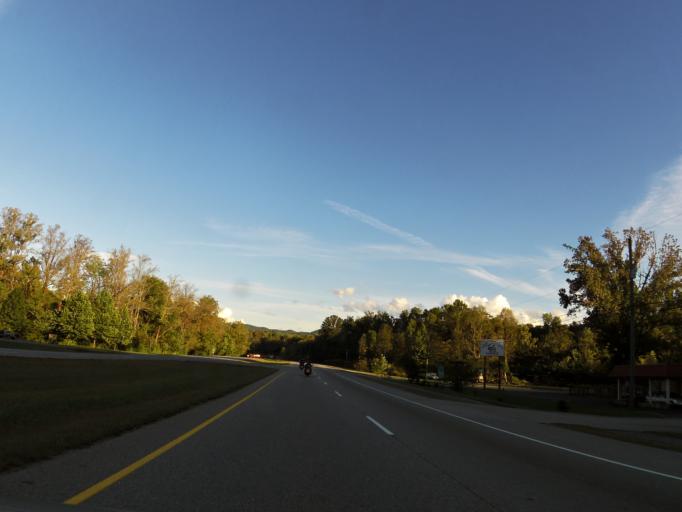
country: US
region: Tennessee
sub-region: Blount County
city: Wildwood
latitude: 35.6822
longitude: -83.7891
